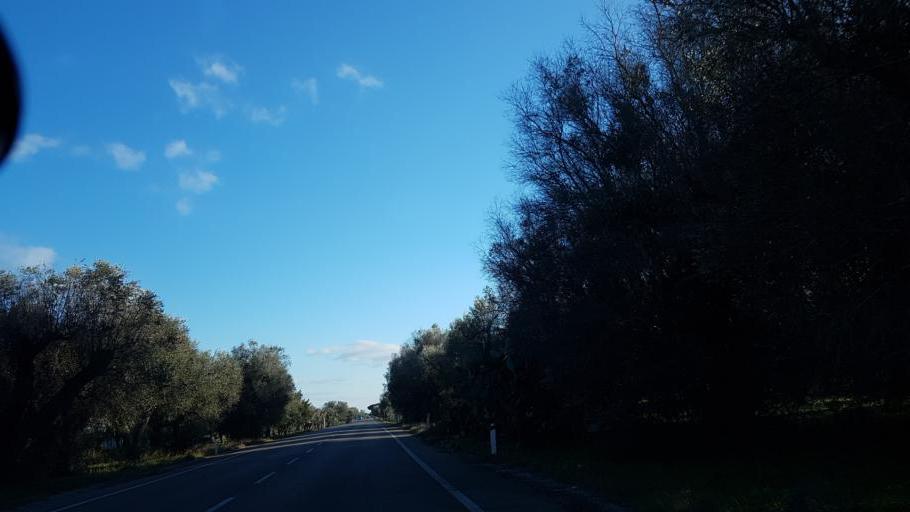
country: IT
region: Apulia
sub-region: Provincia di Lecce
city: Squinzano
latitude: 40.4583
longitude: 18.0224
